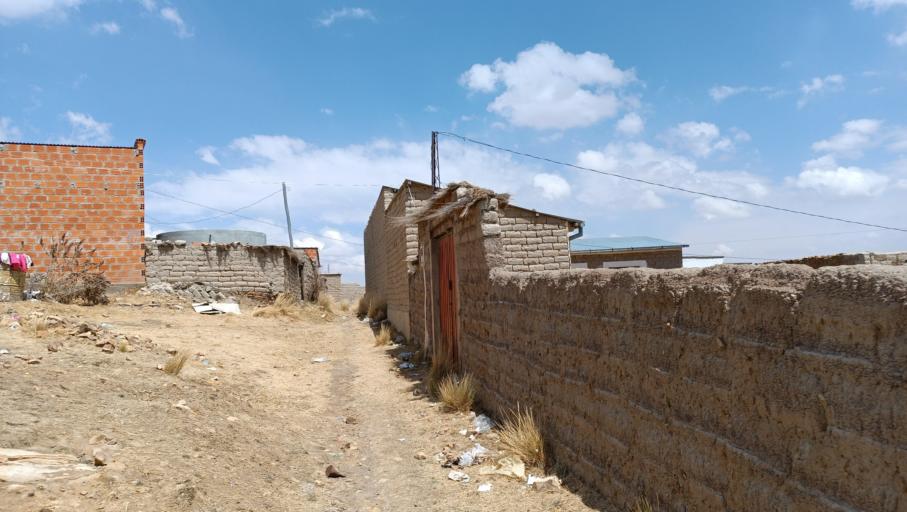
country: BO
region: La Paz
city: Batallas
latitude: -16.3850
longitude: -68.5960
